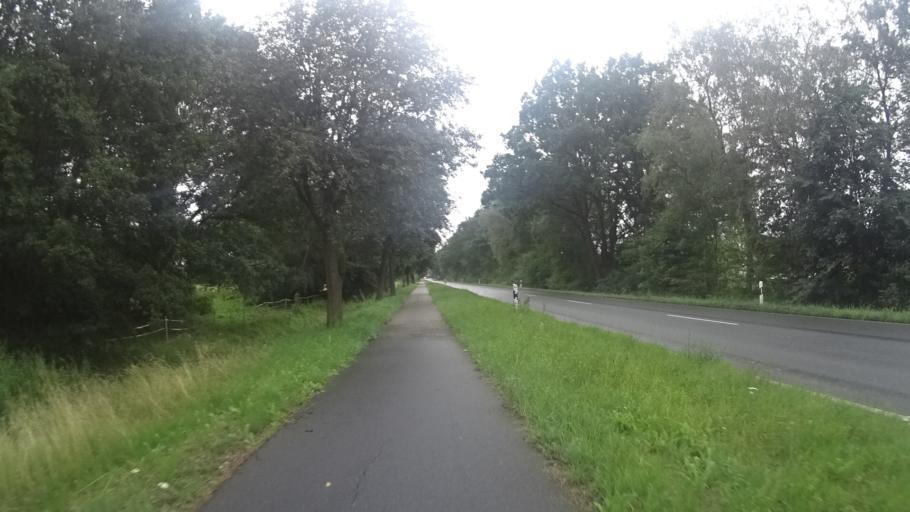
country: DE
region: Schleswig-Holstein
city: Elmshorn
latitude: 53.7716
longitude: 9.6726
